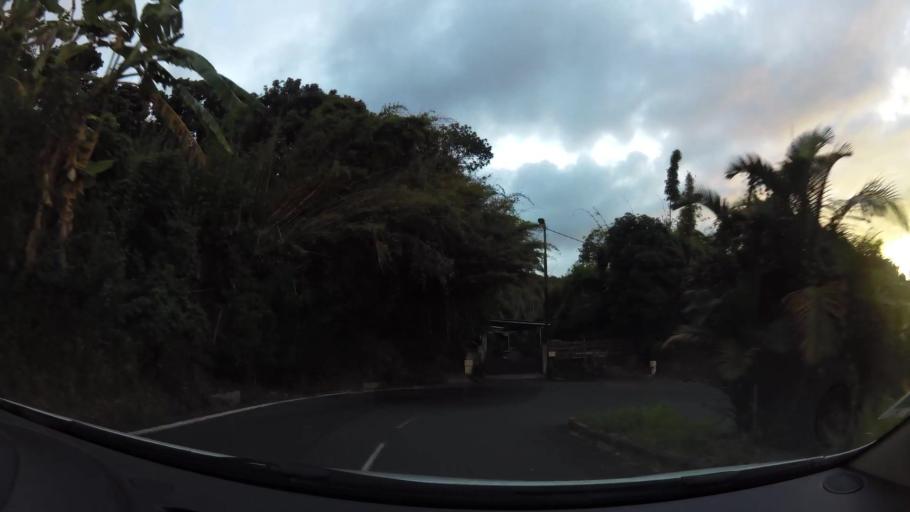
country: RE
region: Reunion
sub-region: Reunion
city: Saint-Denis
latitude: -20.9148
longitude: 55.4602
